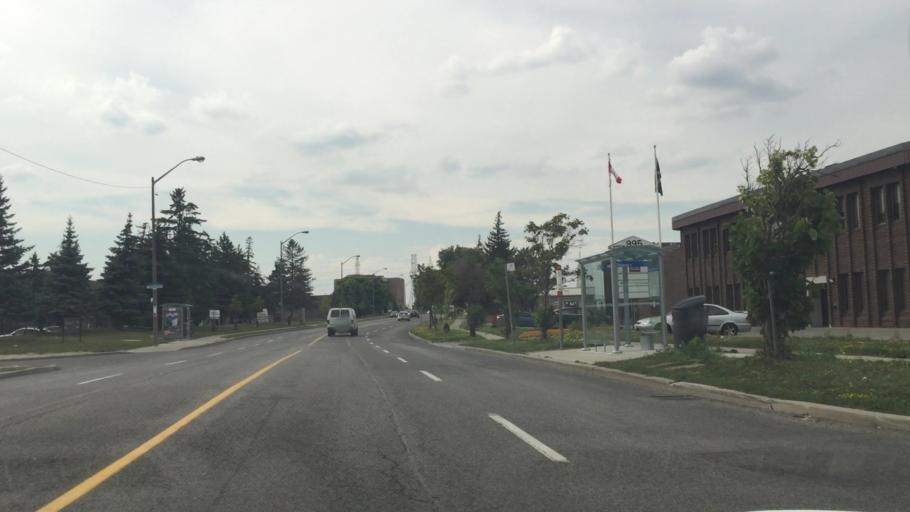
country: CA
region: Ontario
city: Concord
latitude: 43.7492
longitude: -79.5324
